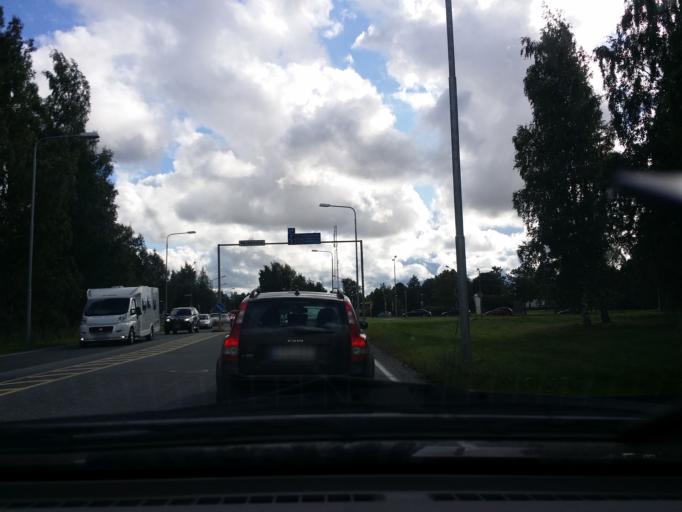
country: FI
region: Satakunta
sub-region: Pori
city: Pori
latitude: 61.4770
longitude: 21.8155
